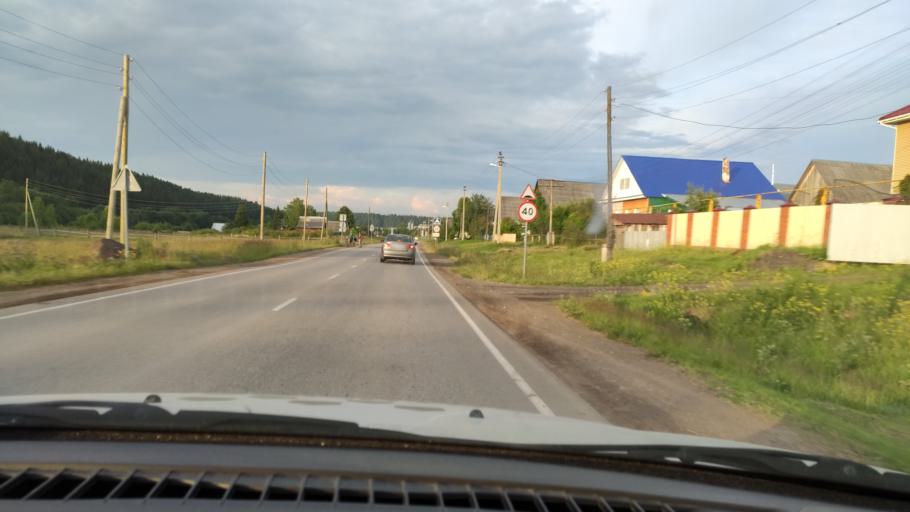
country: RU
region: Perm
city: Kukushtan
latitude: 57.4487
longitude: 56.5013
